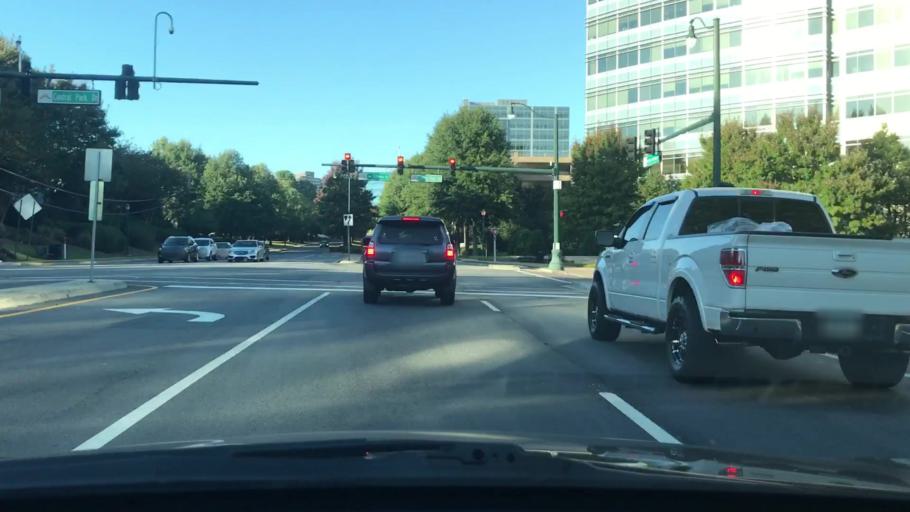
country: US
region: Georgia
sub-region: Fulton County
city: Sandy Springs
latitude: 33.9238
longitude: -84.3513
